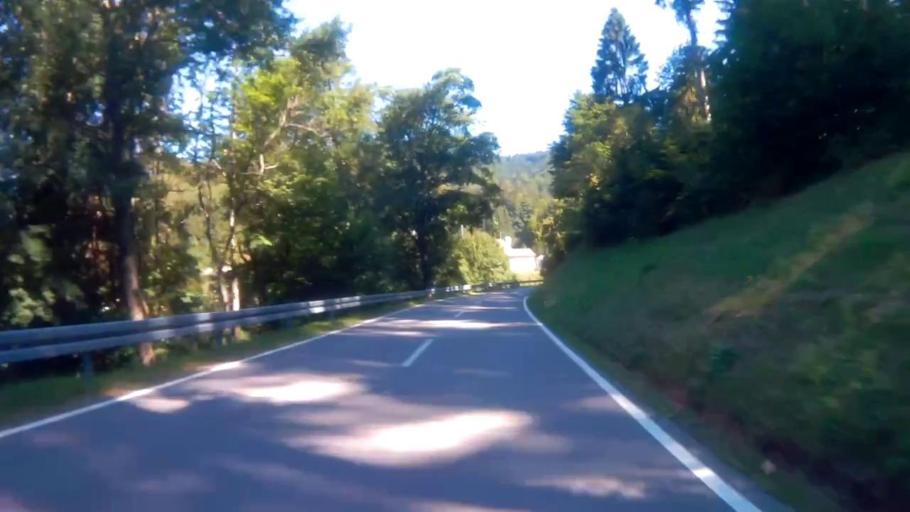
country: DE
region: Baden-Wuerttemberg
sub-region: Freiburg Region
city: Sulzburg
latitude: 47.7802
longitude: 7.7358
